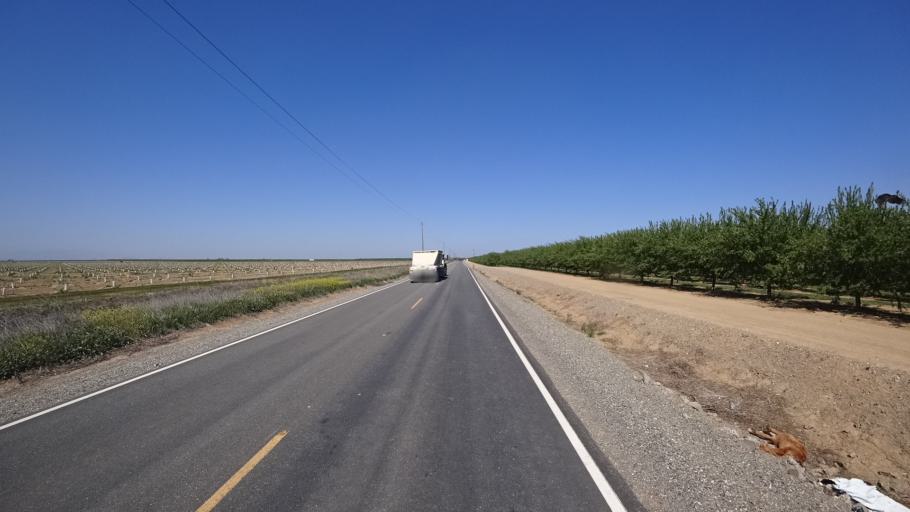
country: US
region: California
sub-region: Glenn County
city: Willows
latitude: 39.6147
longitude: -122.1376
